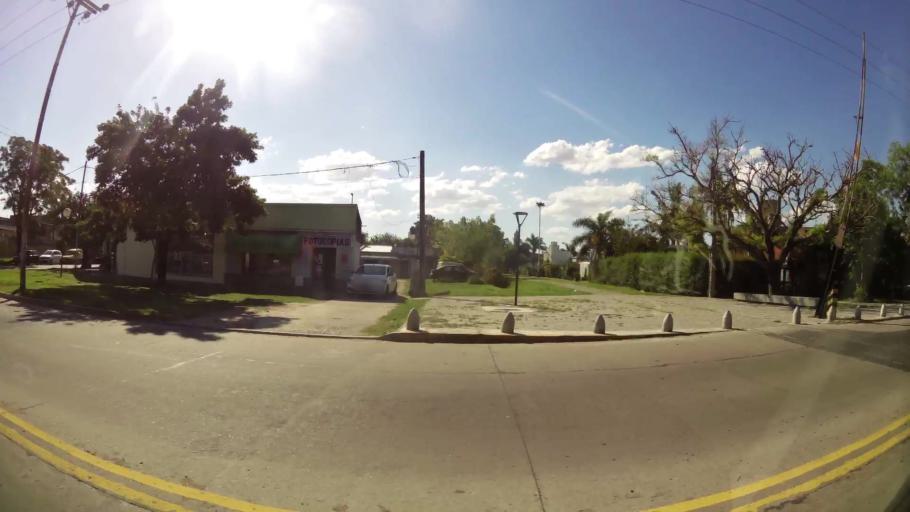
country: AR
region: Santa Fe
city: Santa Fe de la Vera Cruz
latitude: -31.6146
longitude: -60.6816
